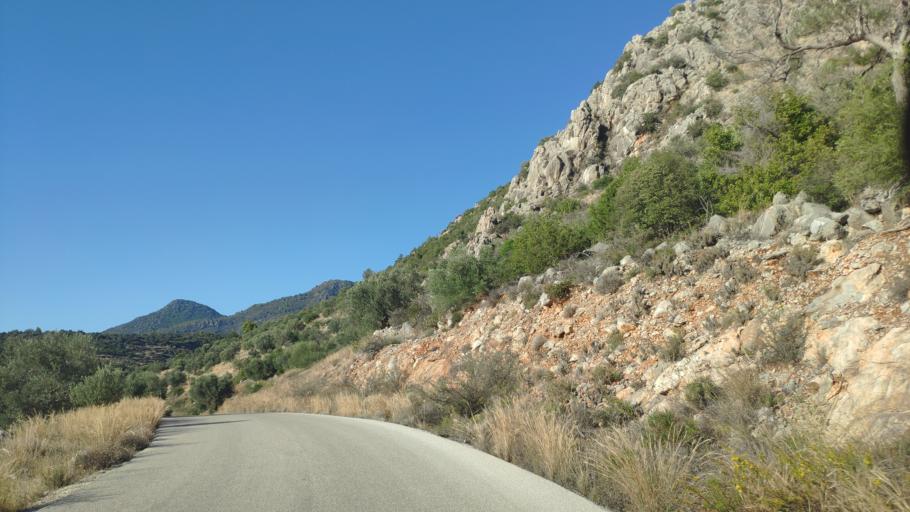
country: GR
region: Attica
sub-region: Nomos Piraios
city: Galatas
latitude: 37.5757
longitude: 23.3602
